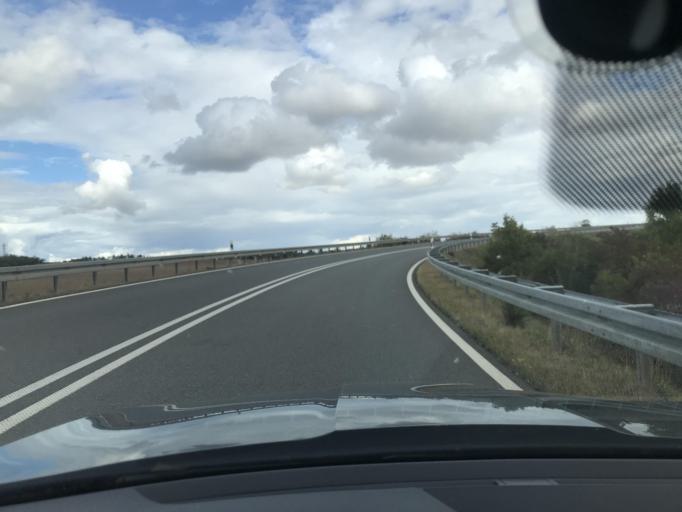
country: DE
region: Saxony-Anhalt
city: Westerhausen
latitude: 51.8095
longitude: 11.0262
